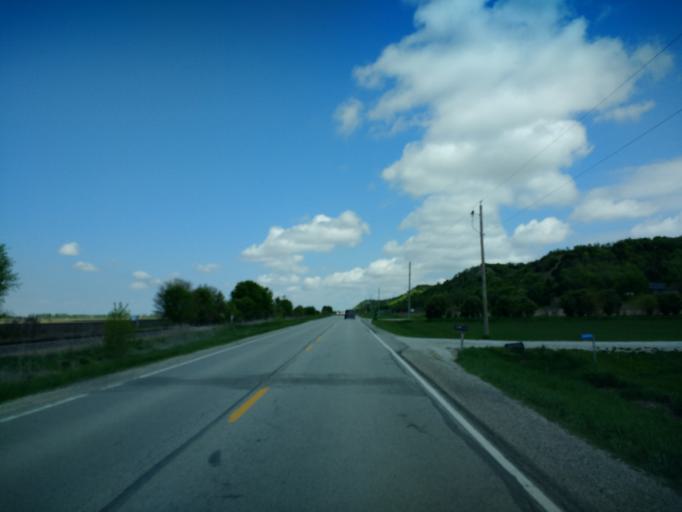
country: US
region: Iowa
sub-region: Harrison County
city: Missouri Valley
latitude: 41.4622
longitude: -95.8771
